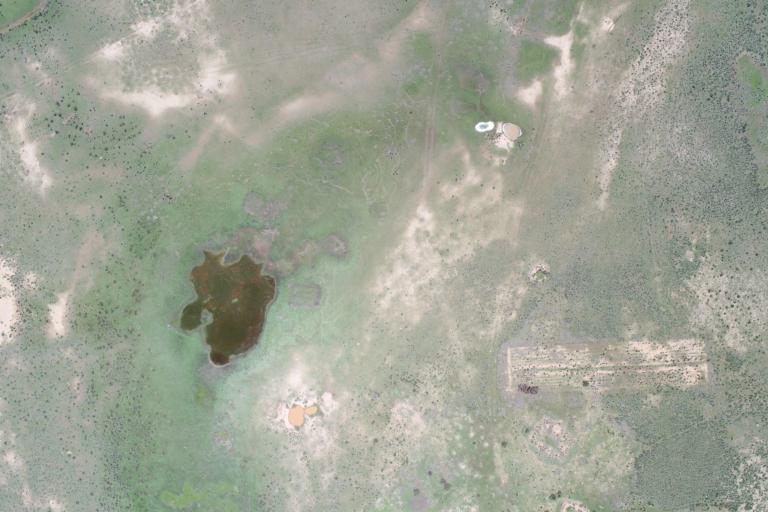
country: BO
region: La Paz
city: Curahuara de Carangas
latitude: -17.3124
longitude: -68.5171
